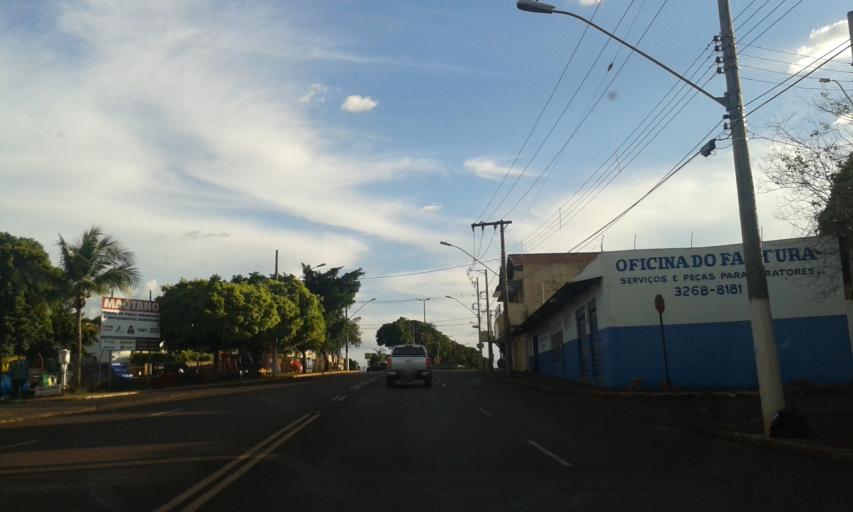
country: BR
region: Minas Gerais
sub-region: Ituiutaba
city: Ituiutaba
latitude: -18.9578
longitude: -49.4570
